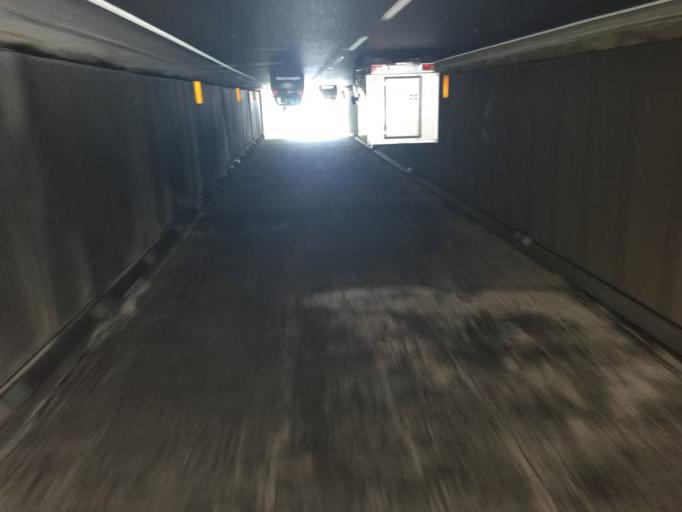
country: IT
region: Tuscany
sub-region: Province of Pisa
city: La Rotta
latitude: 43.6603
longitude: 10.6982
